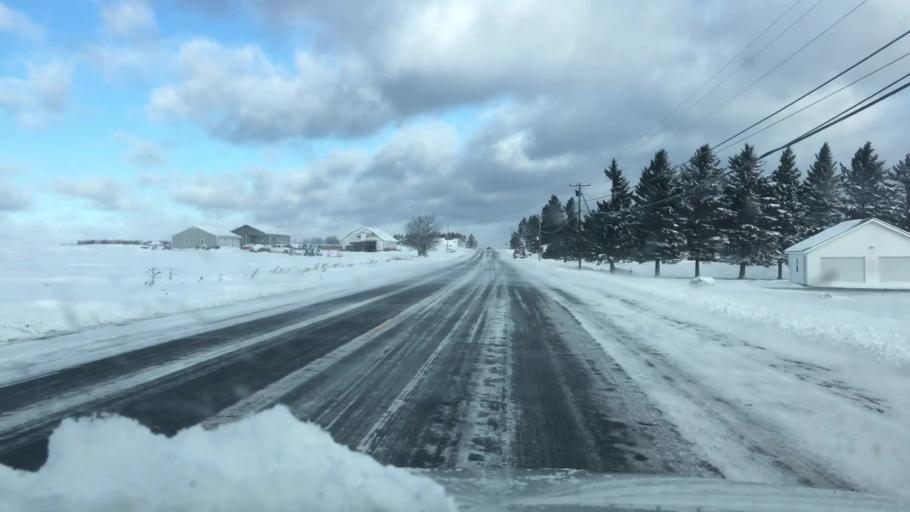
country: US
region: Maine
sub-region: Aroostook County
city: Caribou
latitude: 46.9070
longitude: -68.0162
